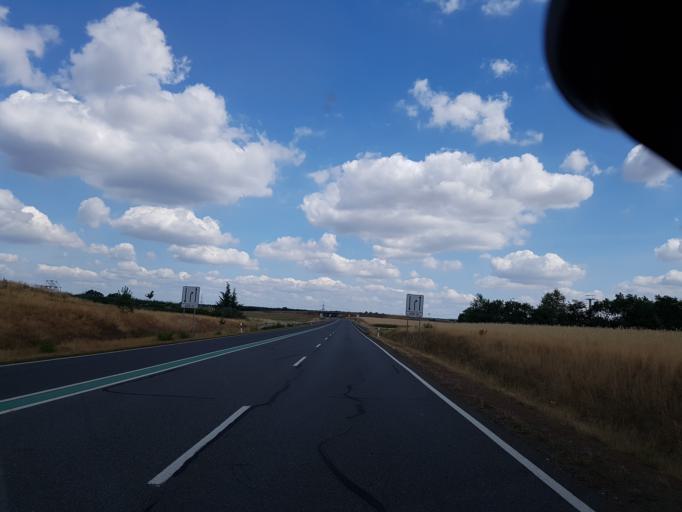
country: DE
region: Brandenburg
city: Drebkau
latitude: 51.6485
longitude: 14.2401
